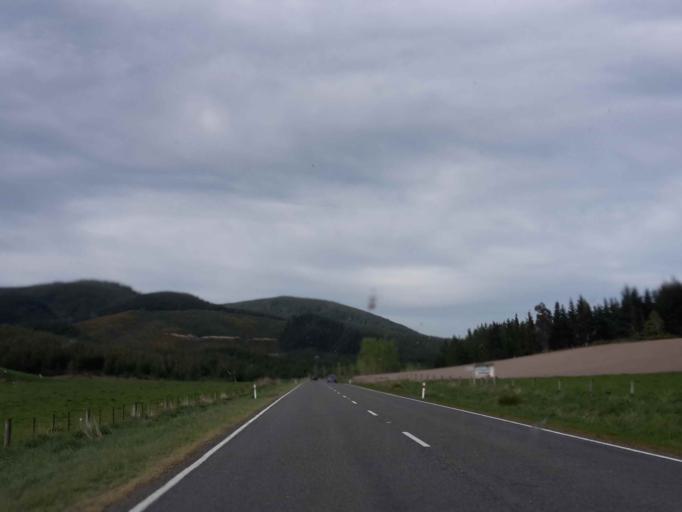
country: NZ
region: Canterbury
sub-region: Timaru District
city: Pleasant Point
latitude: -44.1213
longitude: 171.0507
